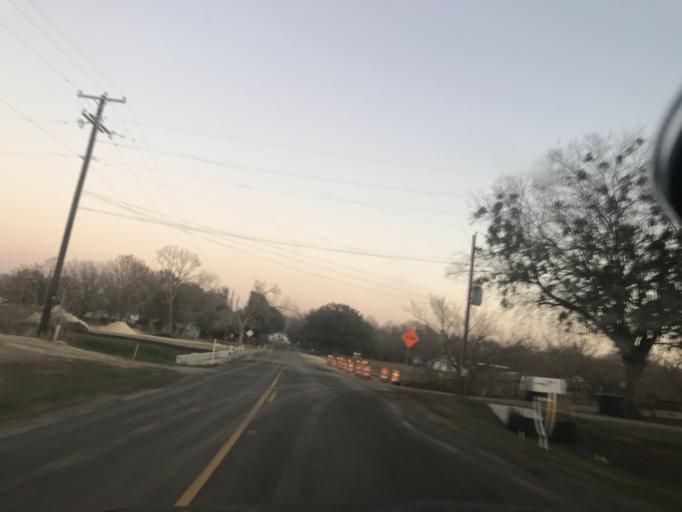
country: US
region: Texas
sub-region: Williamson County
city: Hutto
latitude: 30.4957
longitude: -97.5000
